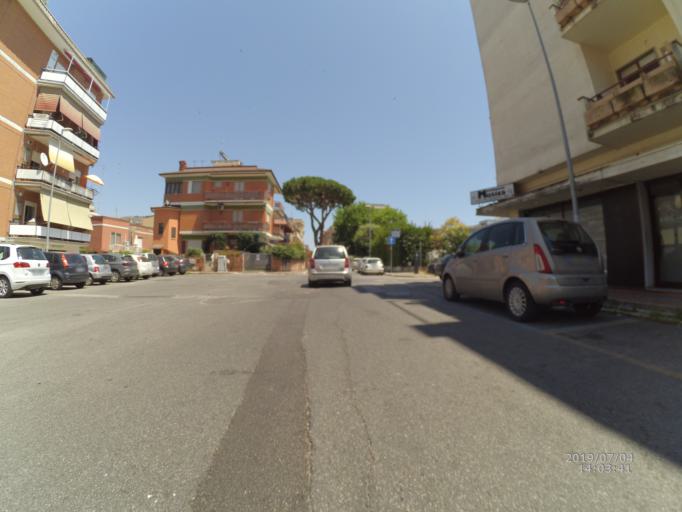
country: IT
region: Latium
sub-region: Provincia di Latina
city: Terracina
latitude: 41.2863
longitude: 13.2415
